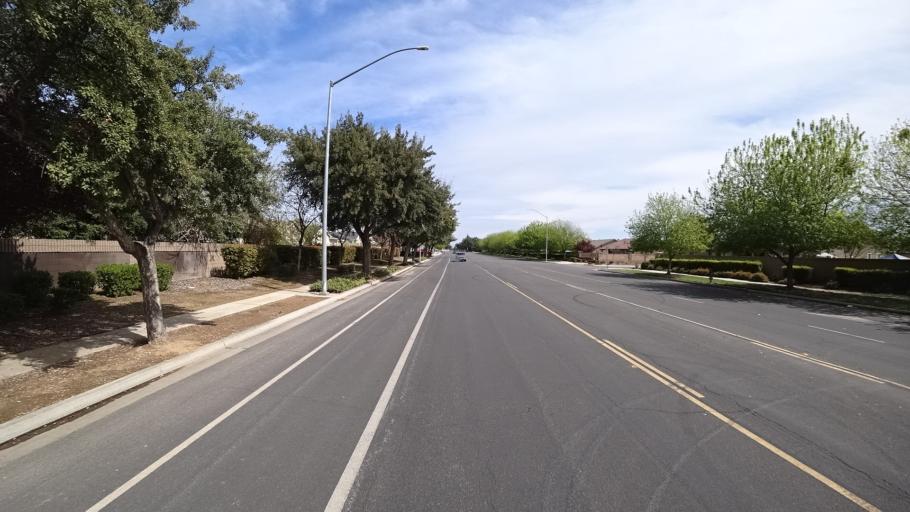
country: US
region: California
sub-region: Fresno County
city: West Park
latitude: 36.8008
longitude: -119.8968
